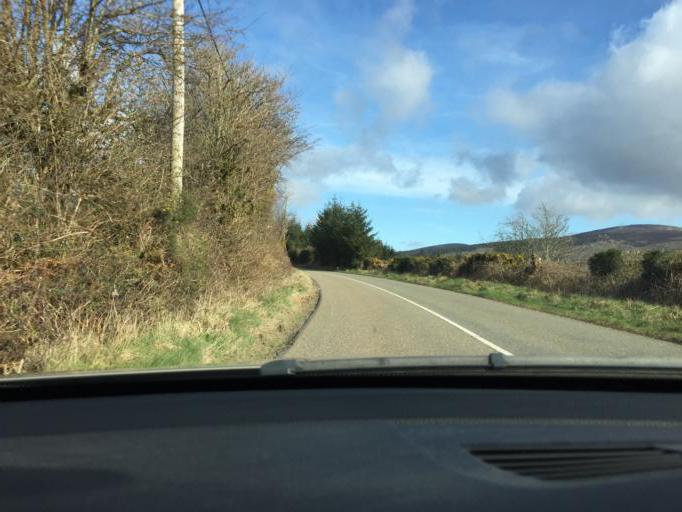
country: IE
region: Leinster
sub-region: Wicklow
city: Valleymount
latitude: 53.0599
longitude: -6.4809
